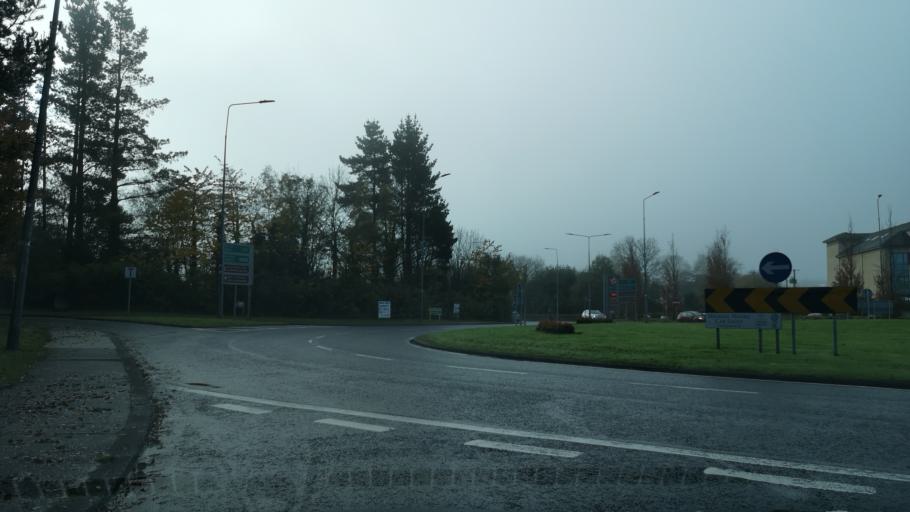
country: IE
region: Leinster
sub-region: An Iarmhi
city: Athlone
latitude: 53.4114
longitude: -7.8919
